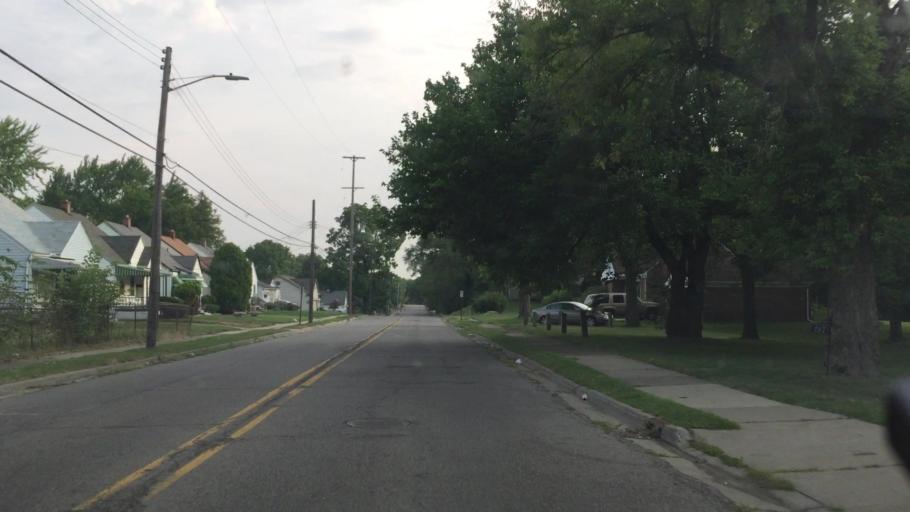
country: US
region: Michigan
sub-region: Oakland County
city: Pontiac
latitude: 42.6305
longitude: -83.2753
